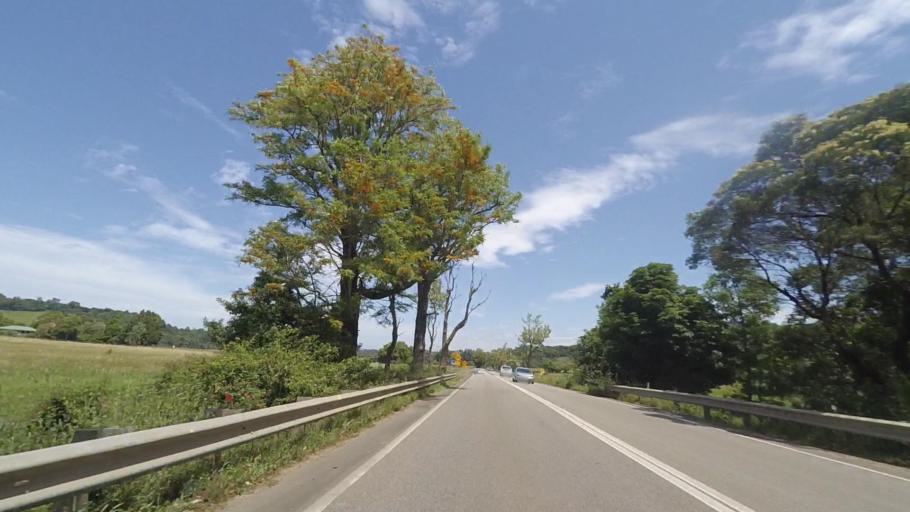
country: AU
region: New South Wales
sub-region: Kiama
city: Gerringong
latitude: -34.7410
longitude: 150.7631
